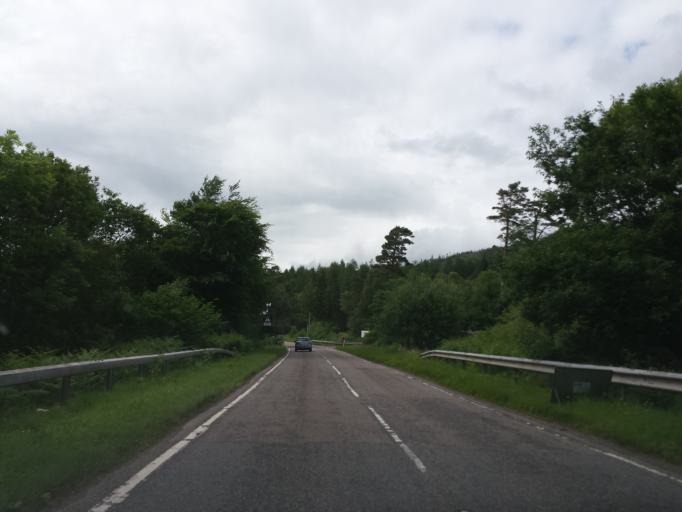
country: GB
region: Scotland
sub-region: Highland
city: Fort William
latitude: 56.8546
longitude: -5.1888
